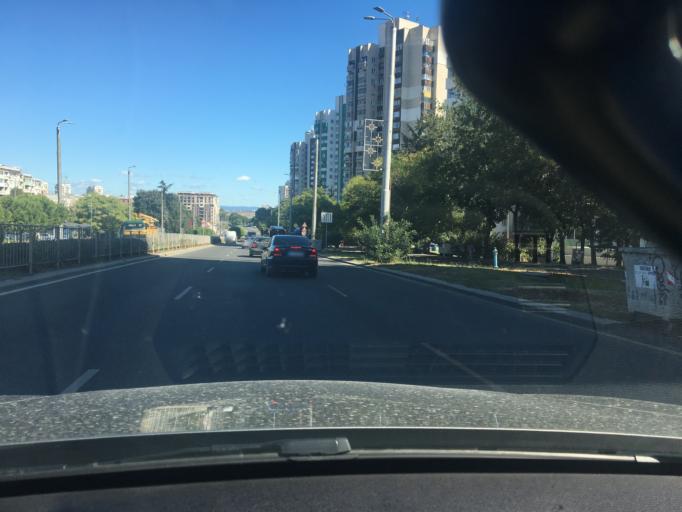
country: BG
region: Burgas
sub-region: Obshtina Burgas
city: Burgas
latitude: 42.5182
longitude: 27.4622
